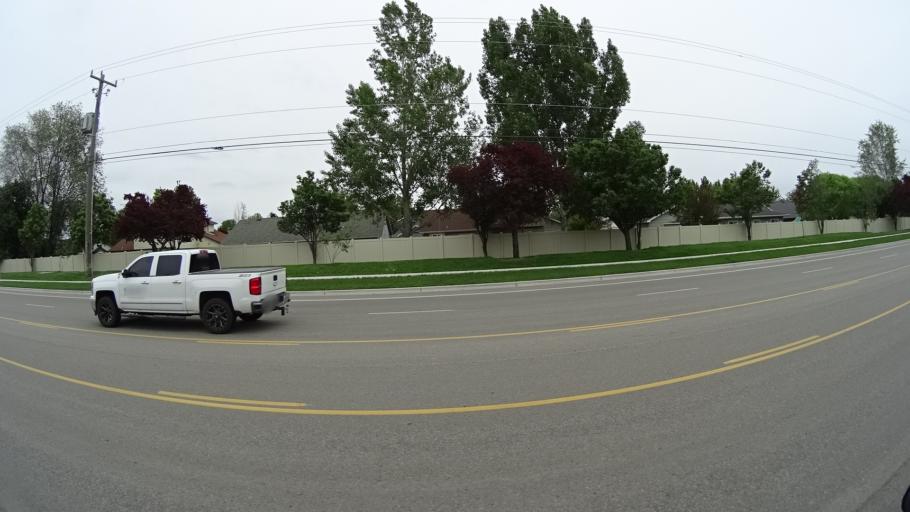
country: US
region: Idaho
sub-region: Ada County
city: Meridian
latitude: 43.6338
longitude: -116.3860
